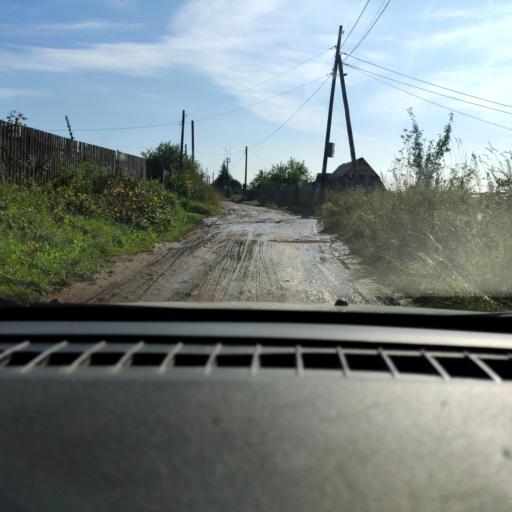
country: RU
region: Perm
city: Novyye Lyady
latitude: 58.0587
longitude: 56.5785
